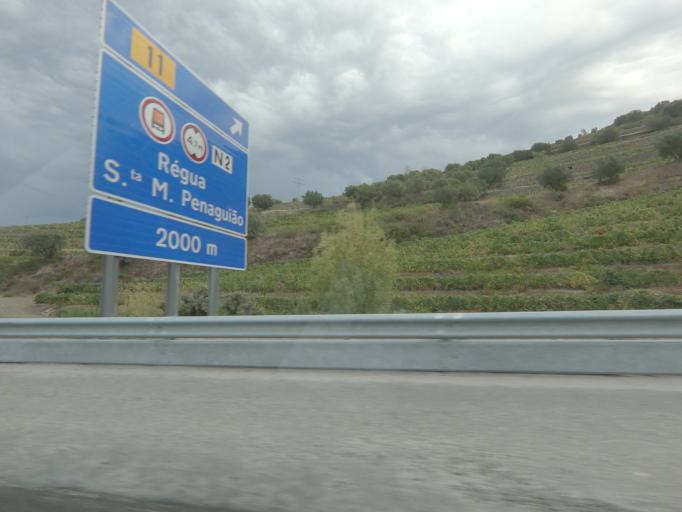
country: PT
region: Vila Real
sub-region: Peso da Regua
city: Peso da Regua
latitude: 41.1482
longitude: -7.7748
